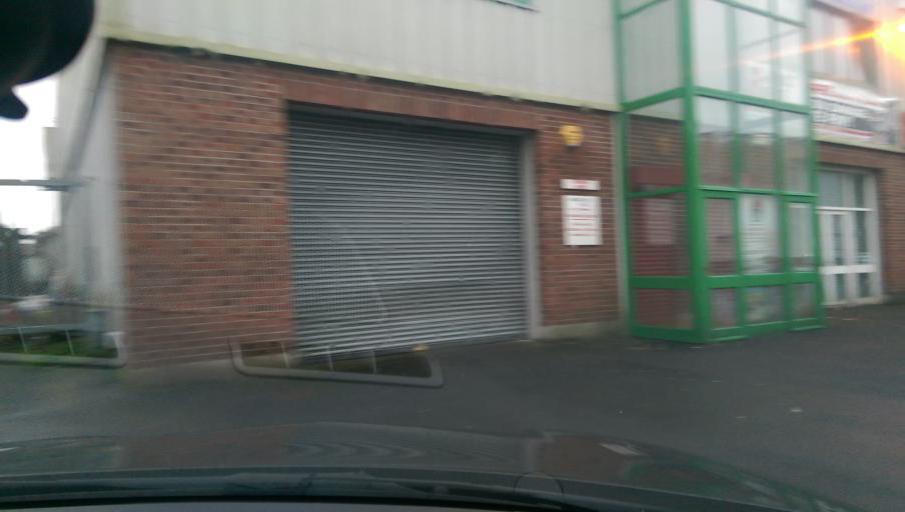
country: IE
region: Connaught
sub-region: County Galway
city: Gaillimh
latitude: 53.2844
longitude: -9.0365
